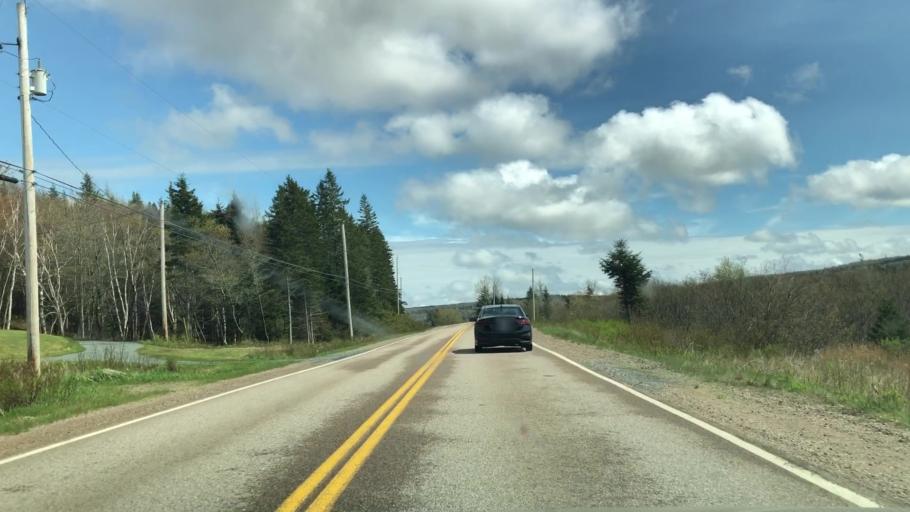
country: CA
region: Nova Scotia
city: Antigonish
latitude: 45.1899
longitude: -61.9892
